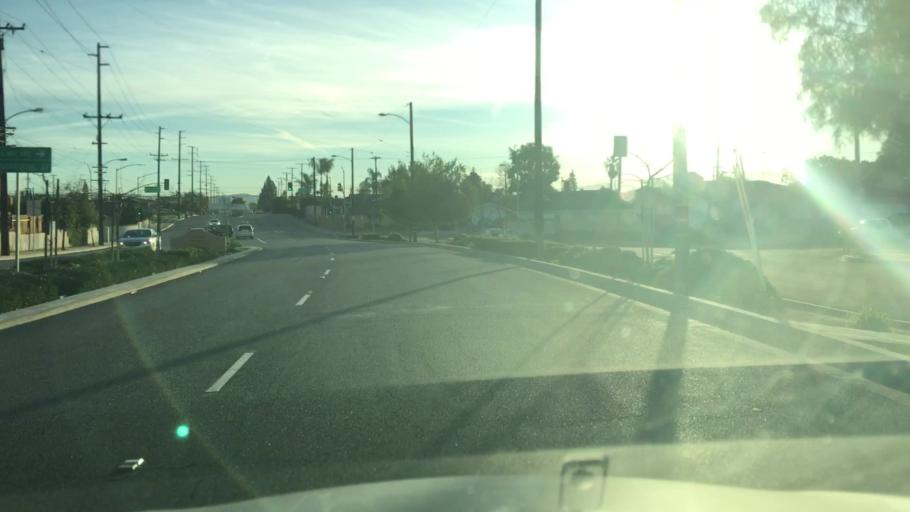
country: US
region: California
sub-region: Los Angeles County
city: East La Mirada
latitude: 33.9246
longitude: -117.9784
